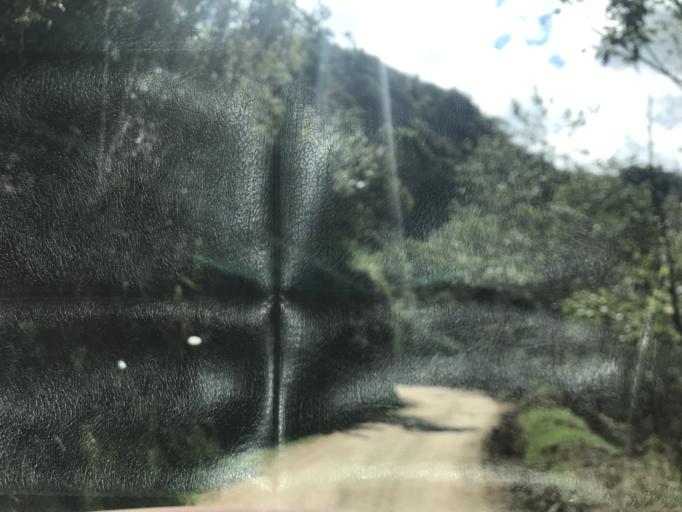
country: PE
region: Cajamarca
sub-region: Provincia de Chota
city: Querocoto
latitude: -6.3523
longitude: -79.0453
